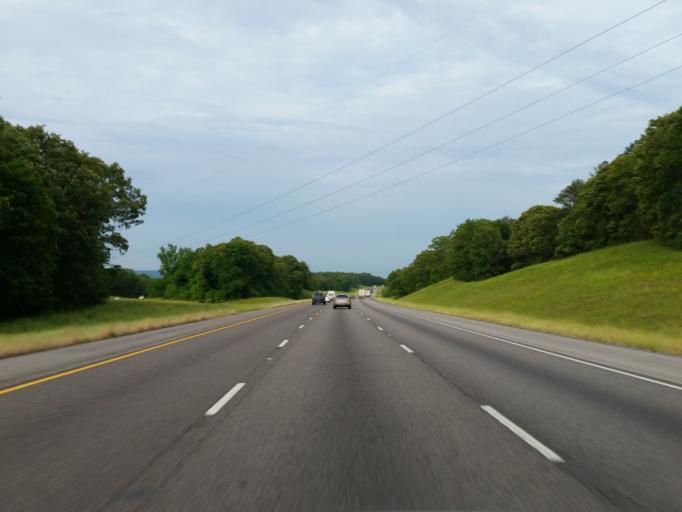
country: US
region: Alabama
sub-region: Calhoun County
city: Bynum
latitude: 33.5769
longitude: -85.9817
